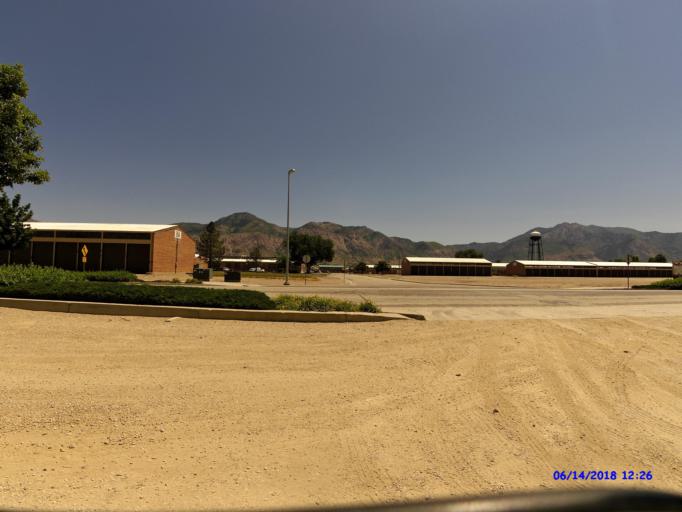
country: US
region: Utah
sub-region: Weber County
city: Harrisville
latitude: 41.2612
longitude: -111.9985
